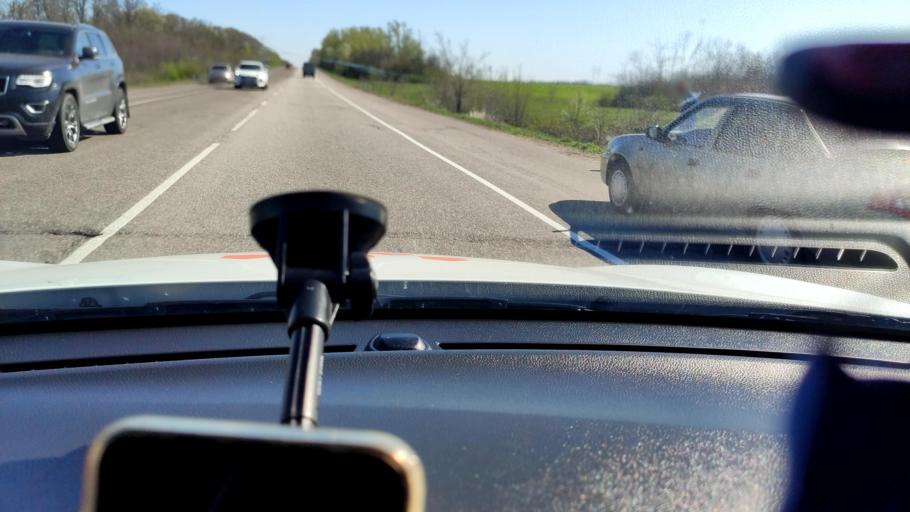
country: RU
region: Voronezj
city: Kolodeznyy
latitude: 51.2655
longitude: 39.0507
